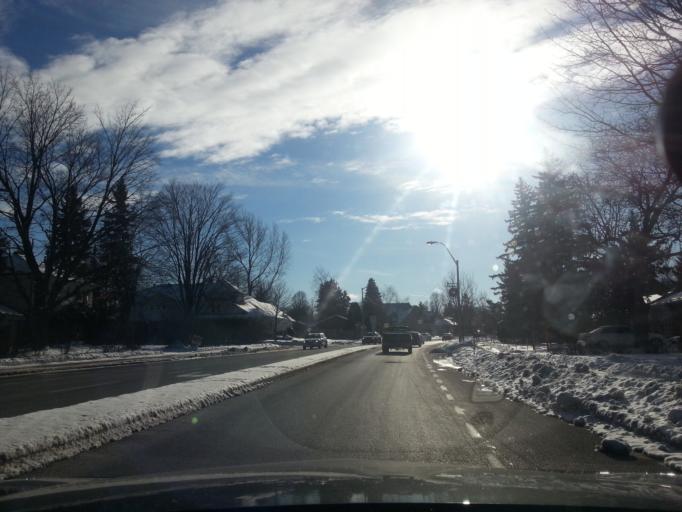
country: CA
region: Ontario
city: Ottawa
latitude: 45.3983
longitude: -75.6617
